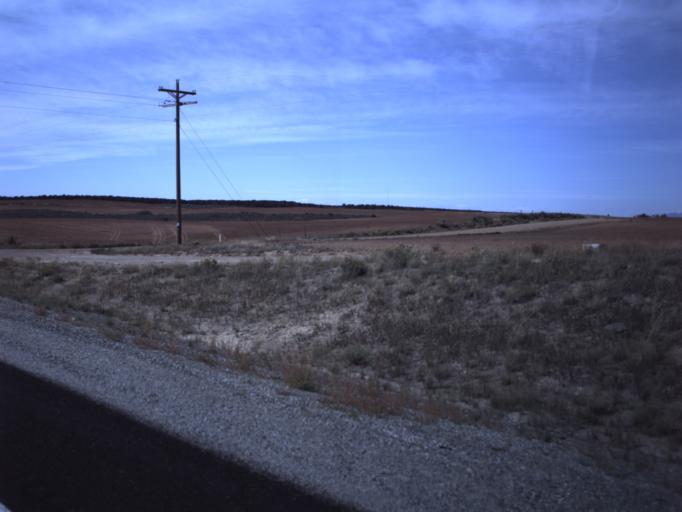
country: US
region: Utah
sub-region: San Juan County
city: Monticello
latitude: 37.8434
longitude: -109.1355
